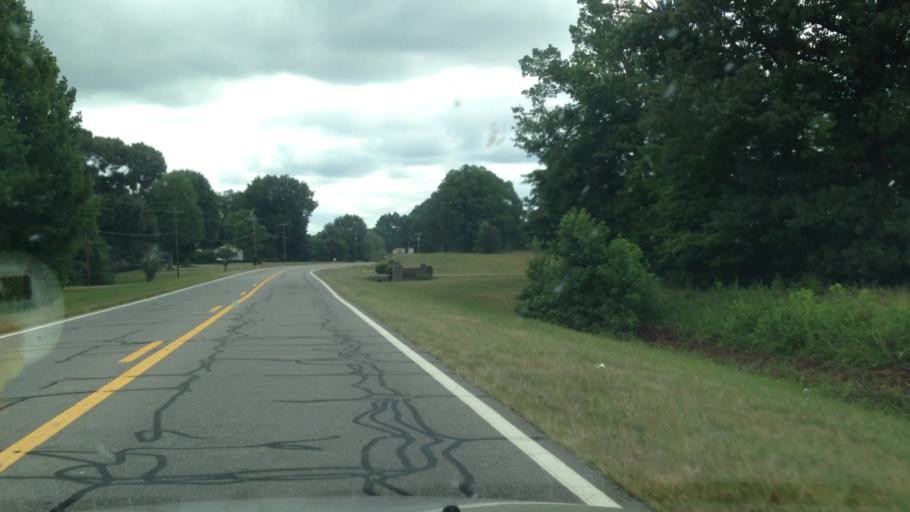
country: US
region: North Carolina
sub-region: Rockingham County
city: Madison
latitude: 36.3791
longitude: -79.9274
